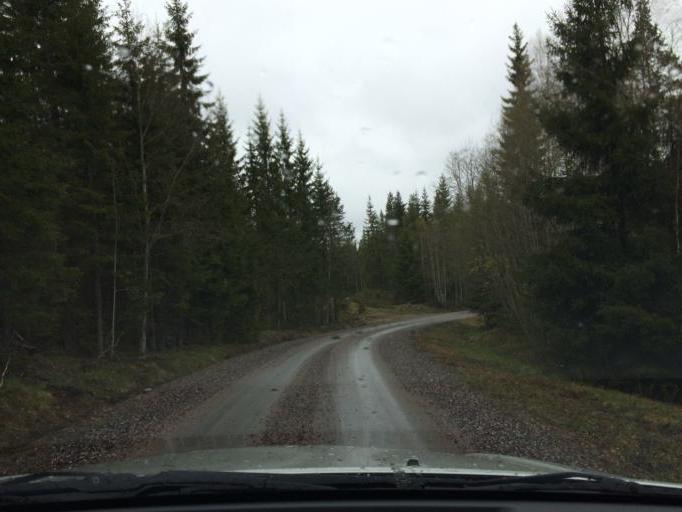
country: SE
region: Dalarna
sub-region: Ludvika Kommun
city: Abborrberget
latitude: 60.0230
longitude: 14.6046
